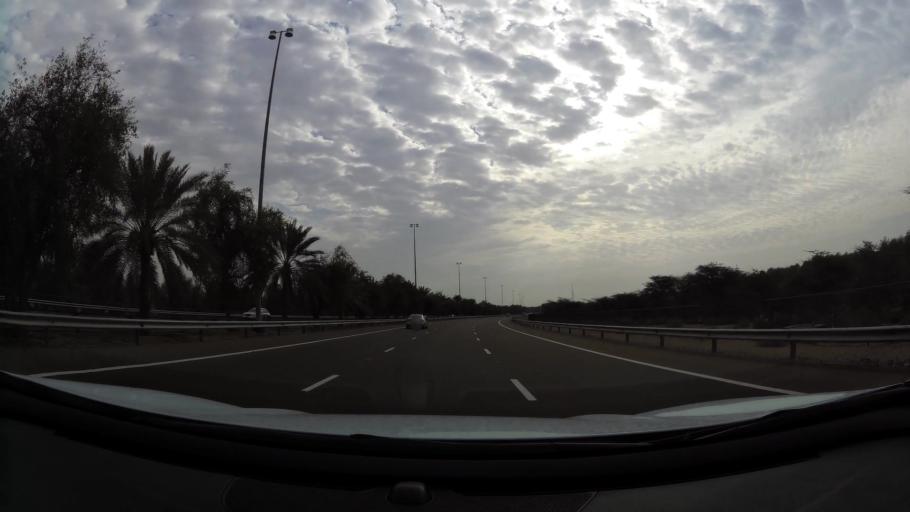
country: AE
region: Abu Dhabi
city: Al Ain
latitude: 24.1696
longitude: 55.2499
